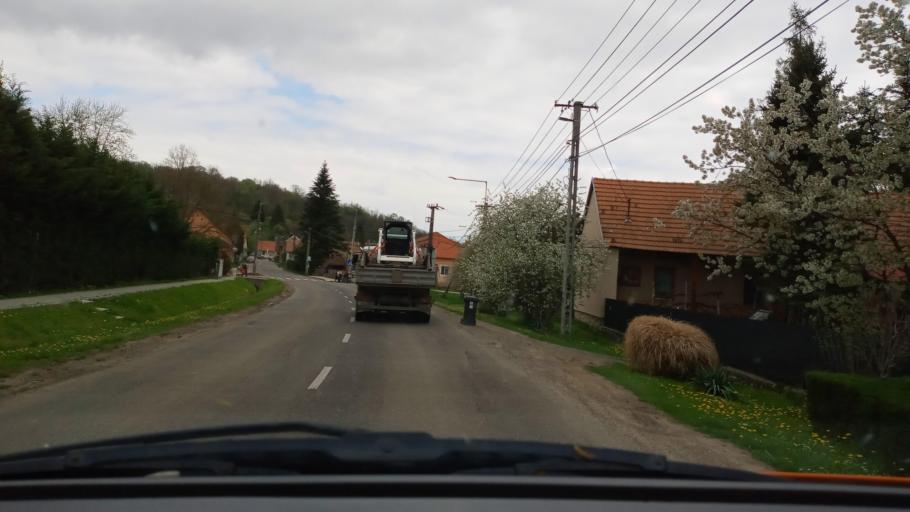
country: HU
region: Baranya
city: Komlo
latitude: 46.2484
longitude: 18.3082
